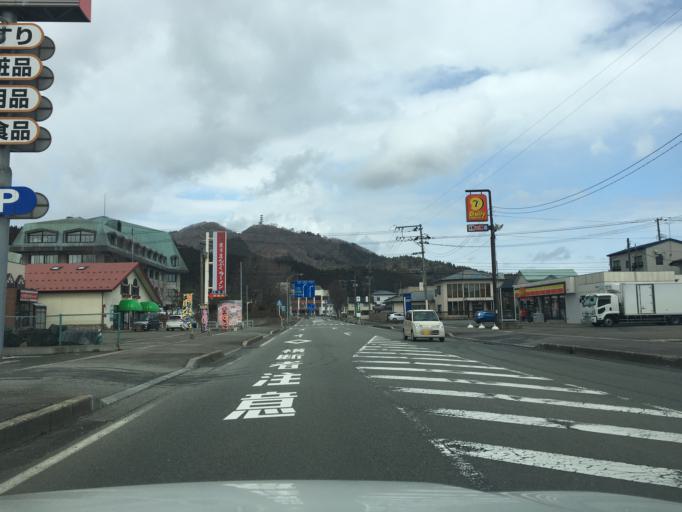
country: JP
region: Akita
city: Tenno
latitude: 39.9424
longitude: 140.1122
